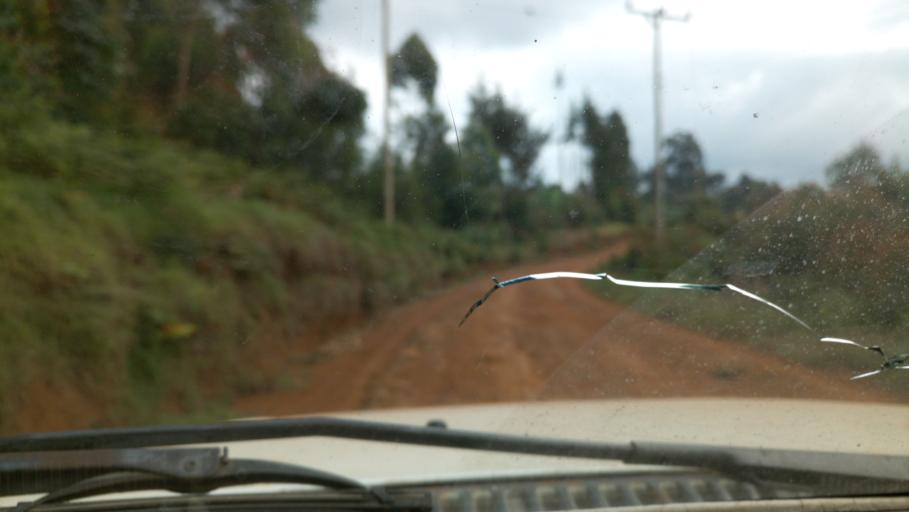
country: KE
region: Murang'a District
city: Kangema
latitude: -0.7615
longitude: 36.8900
